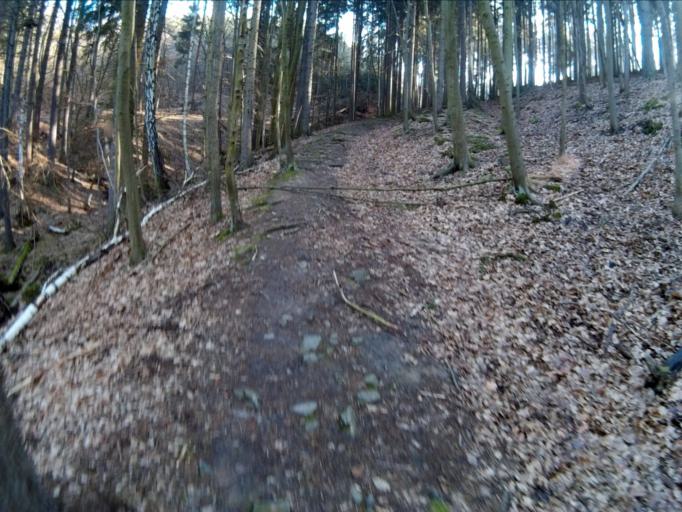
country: CZ
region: Vysocina
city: Namest' nad Oslavou
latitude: 49.1683
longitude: 16.1741
